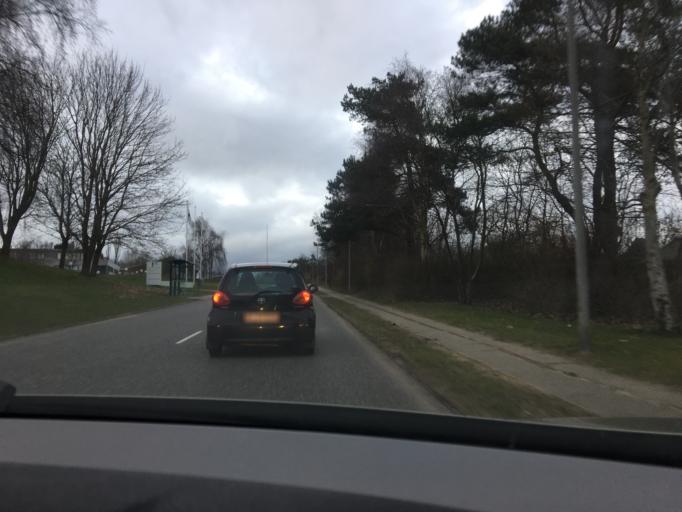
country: DK
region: South Denmark
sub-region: Vejle Kommune
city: Vejle
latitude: 55.7224
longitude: 9.5969
